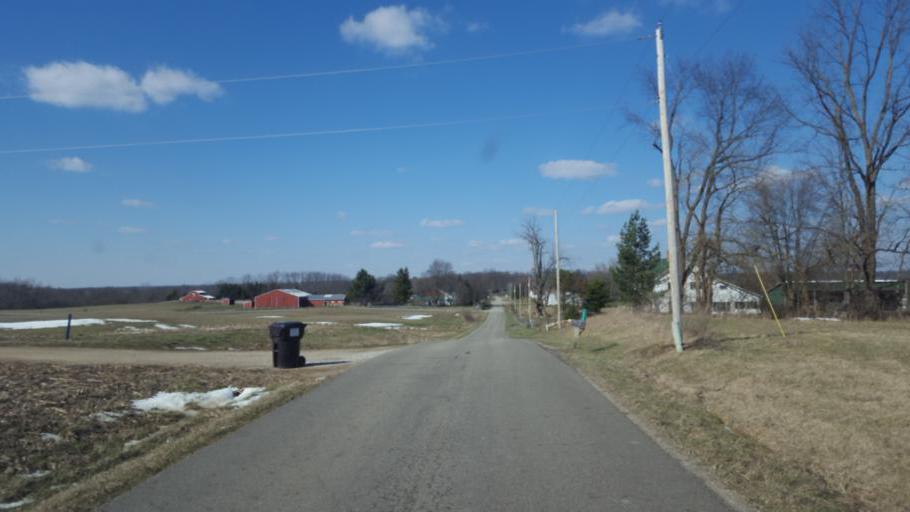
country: US
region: Ohio
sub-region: Knox County
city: Fredericktown
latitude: 40.4495
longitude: -82.6778
